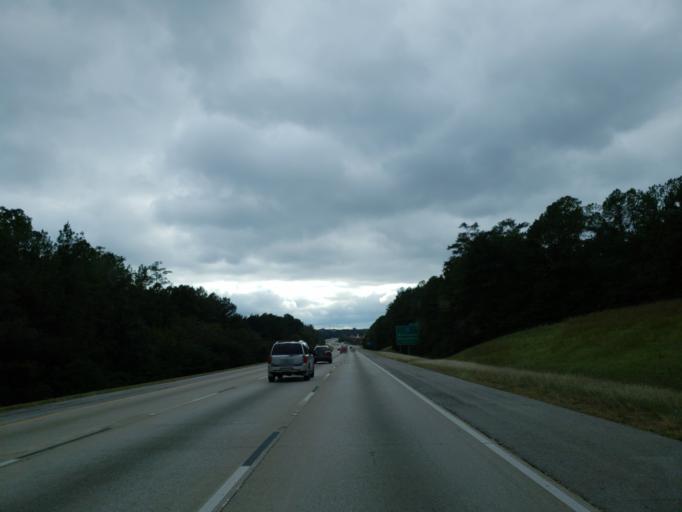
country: US
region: Alabama
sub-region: Jefferson County
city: Vestavia Hills
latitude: 33.4192
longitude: -86.7531
